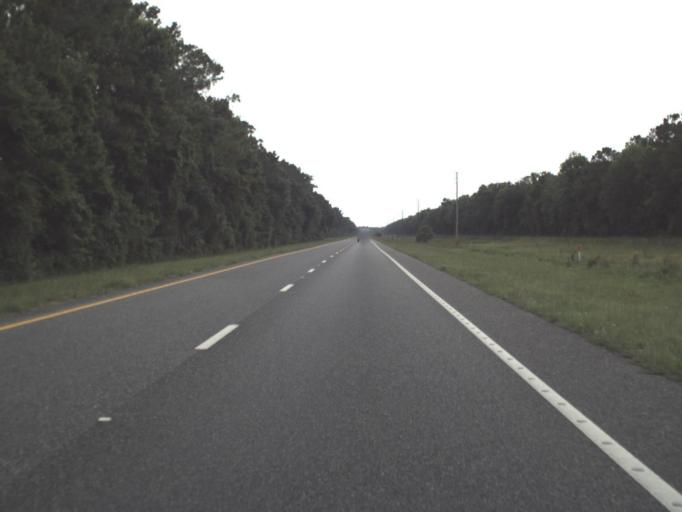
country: US
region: Florida
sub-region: Levy County
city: Inglis
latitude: 29.1753
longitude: -82.6598
